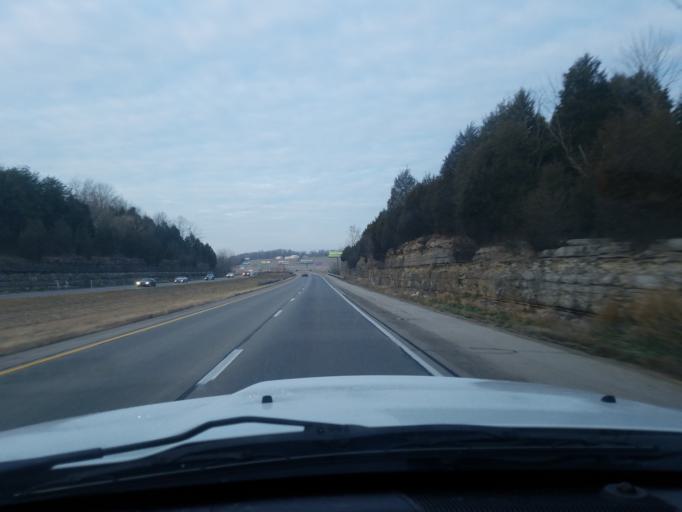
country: US
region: Indiana
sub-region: Harrison County
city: Corydon
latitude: 38.2437
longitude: -86.0996
